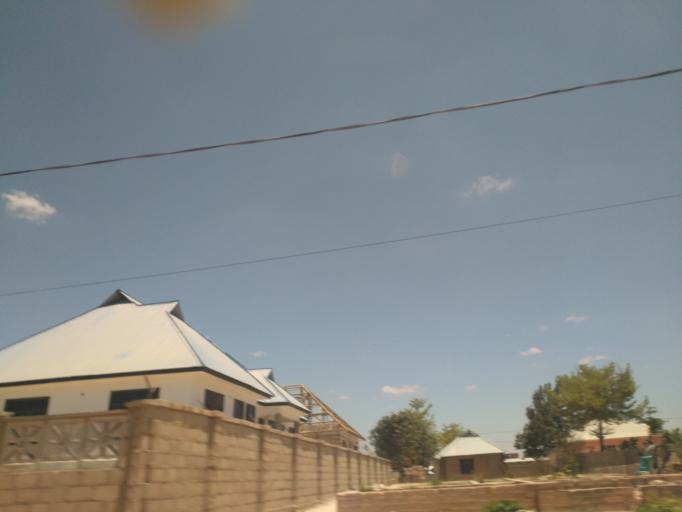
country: TZ
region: Dodoma
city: Dodoma
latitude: -6.1467
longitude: 35.7336
